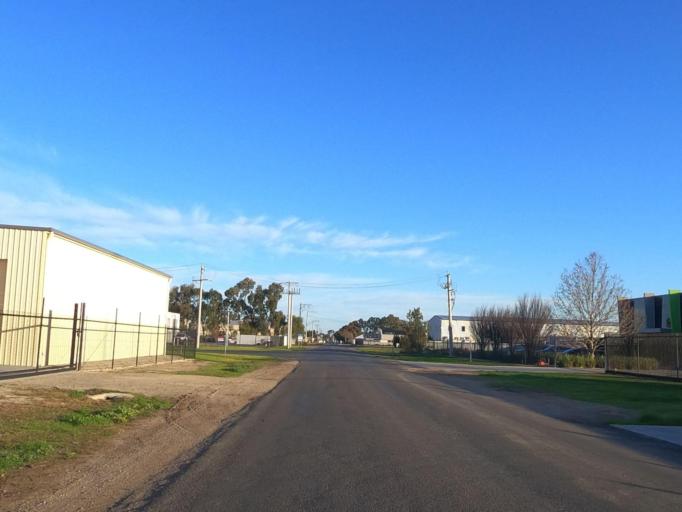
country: AU
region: Victoria
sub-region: Swan Hill
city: Swan Hill
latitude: -35.3264
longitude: 143.5352
